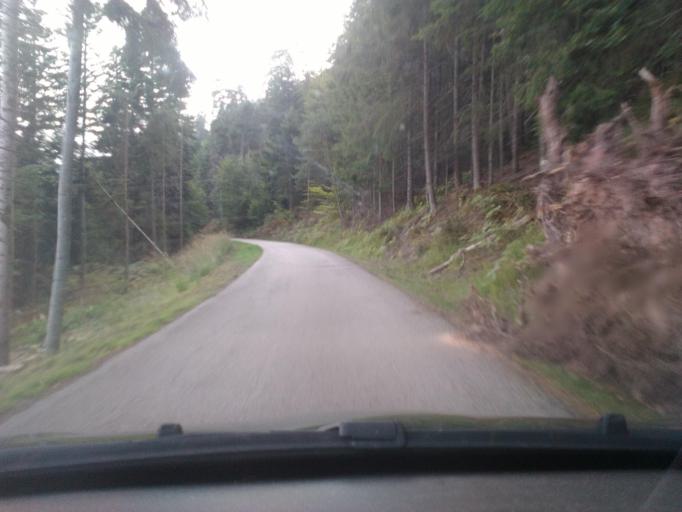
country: FR
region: Lorraine
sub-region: Departement des Vosges
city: Corcieux
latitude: 48.2098
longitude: 6.8798
